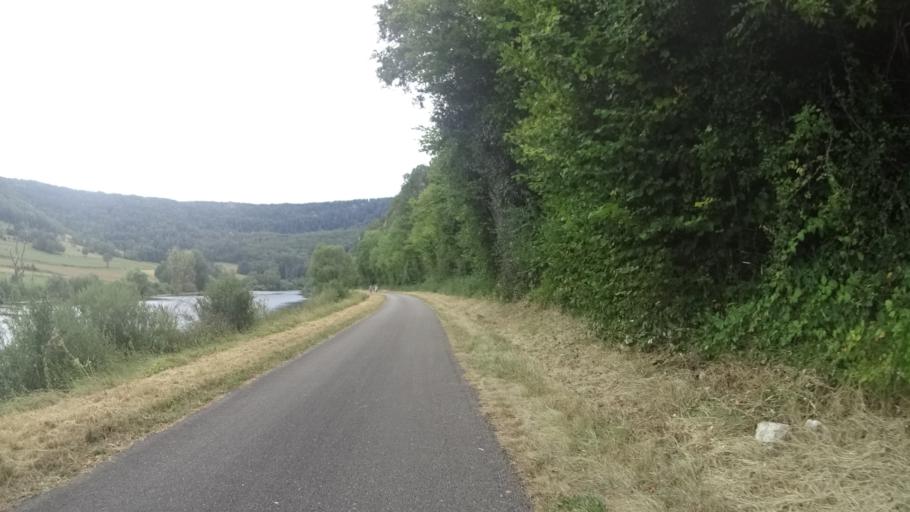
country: FR
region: Franche-Comte
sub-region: Departement du Doubs
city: Baume-les-Dames
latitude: 47.3393
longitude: 6.3158
